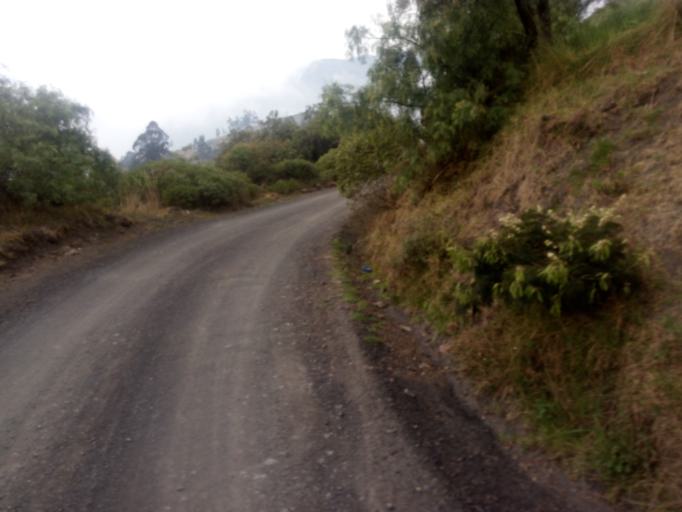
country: CO
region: Boyaca
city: Chita
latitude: 6.1933
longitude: -72.4873
